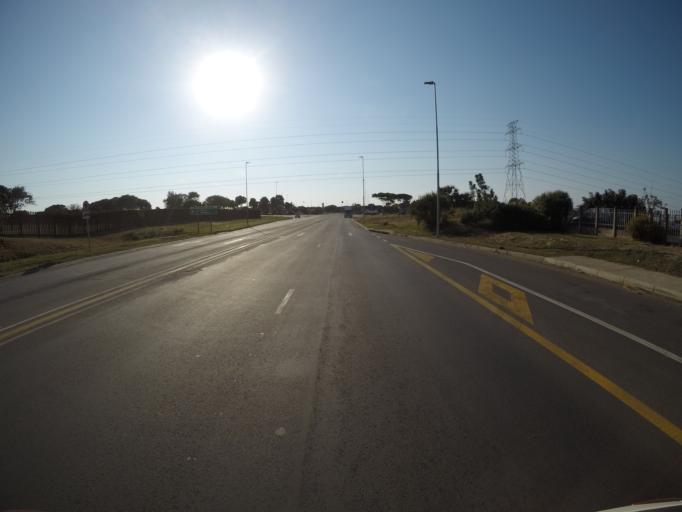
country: ZA
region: KwaZulu-Natal
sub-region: uThungulu District Municipality
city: Richards Bay
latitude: -28.7324
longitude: 32.0374
